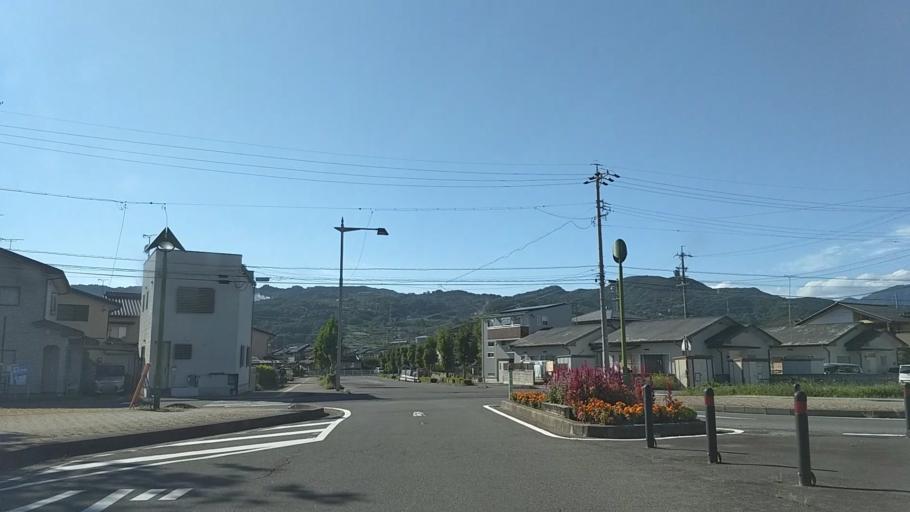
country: JP
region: Nagano
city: Nagano-shi
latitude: 36.5780
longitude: 138.1371
